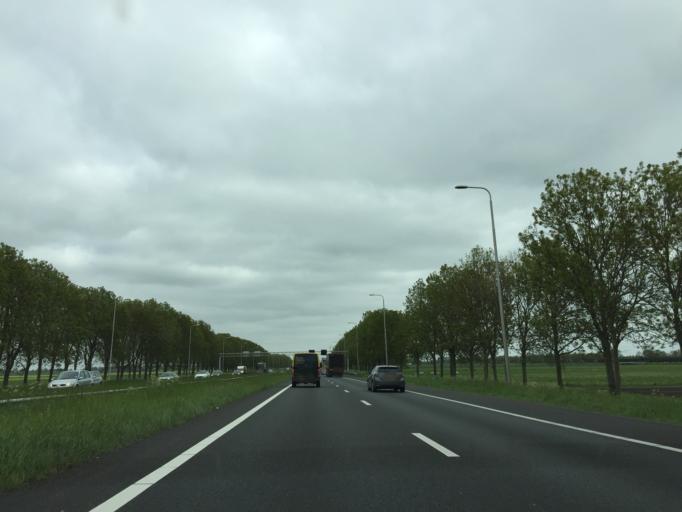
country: NL
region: North Holland
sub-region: Gemeente Beemster
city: Halfweg
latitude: 52.5583
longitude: 4.9639
